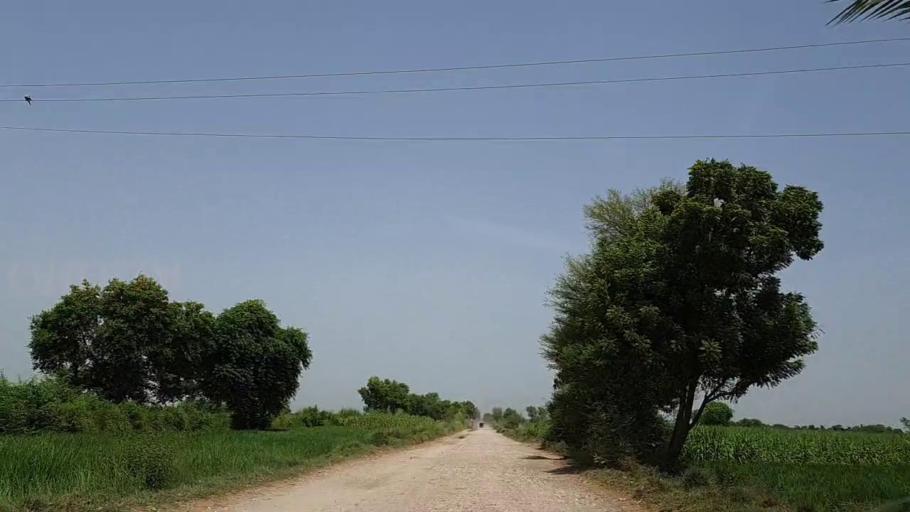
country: PK
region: Sindh
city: Tharu Shah
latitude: 26.8995
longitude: 68.0080
